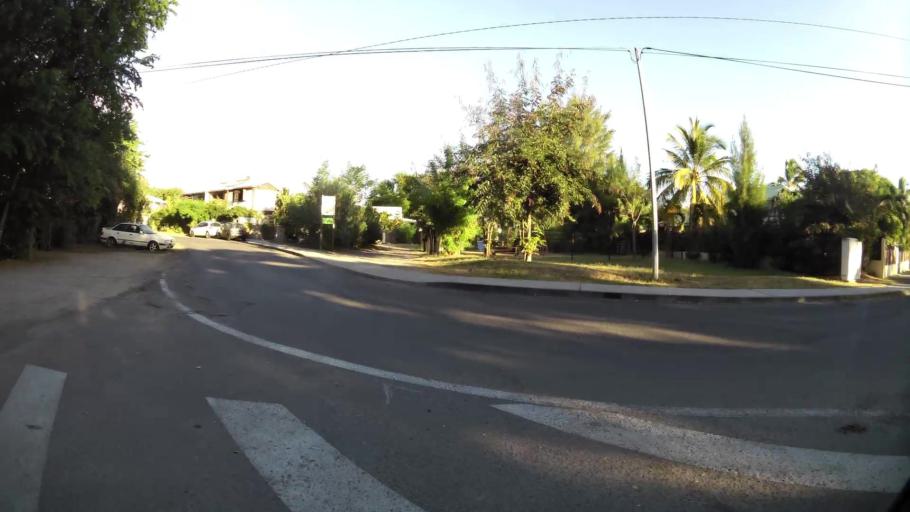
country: RE
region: Reunion
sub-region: Reunion
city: Trois-Bassins
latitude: -21.0942
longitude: 55.2393
